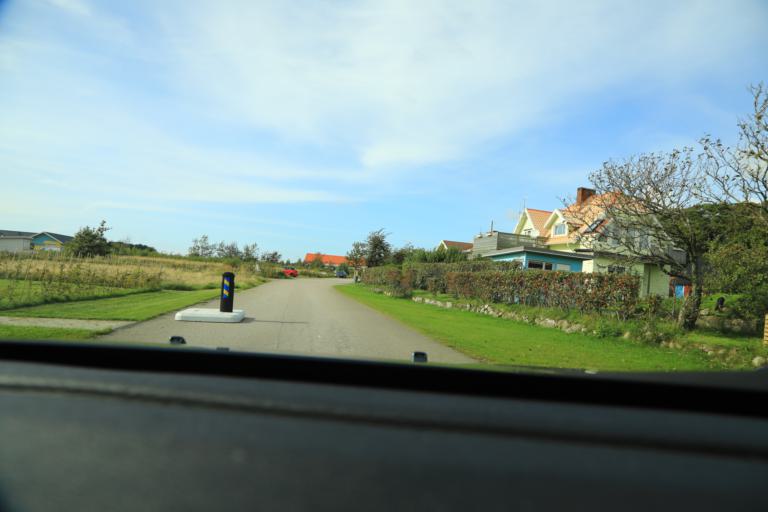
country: SE
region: Halland
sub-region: Varbergs Kommun
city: Traslovslage
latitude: 57.0422
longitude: 12.3180
